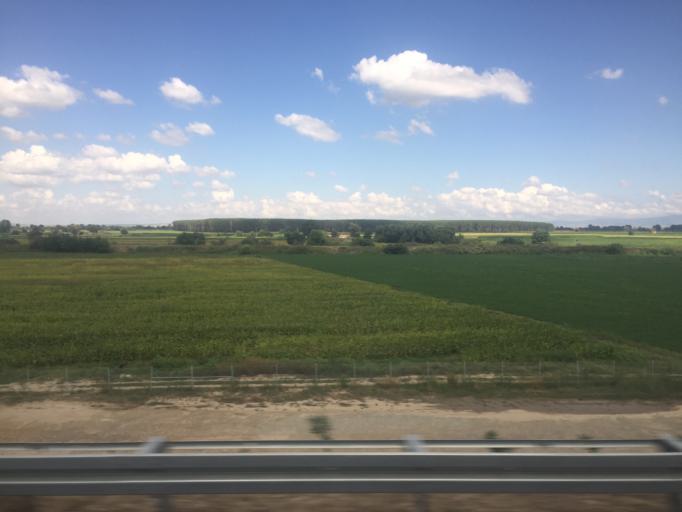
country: TR
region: Bursa
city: Tatkavakli
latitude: 40.0867
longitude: 28.2665
